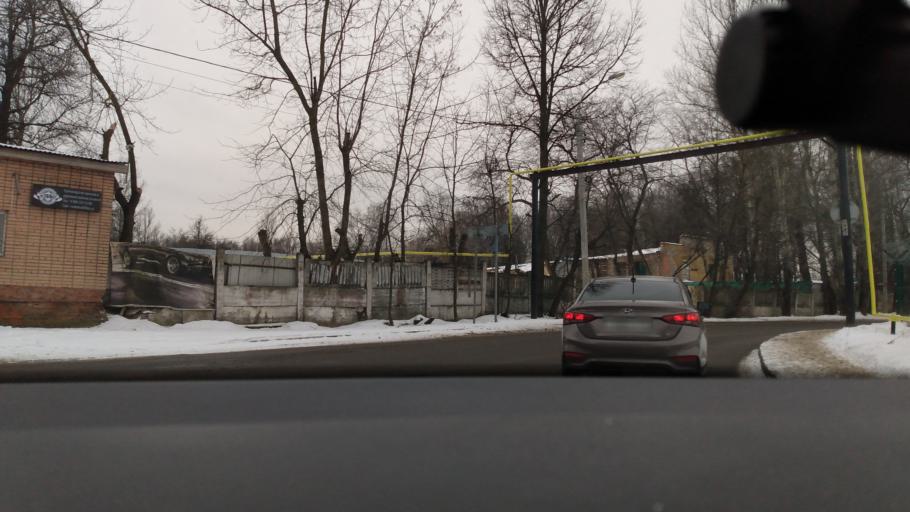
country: RU
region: Moskovskaya
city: Zheleznodorozhnyy
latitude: 55.7352
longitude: 38.0405
